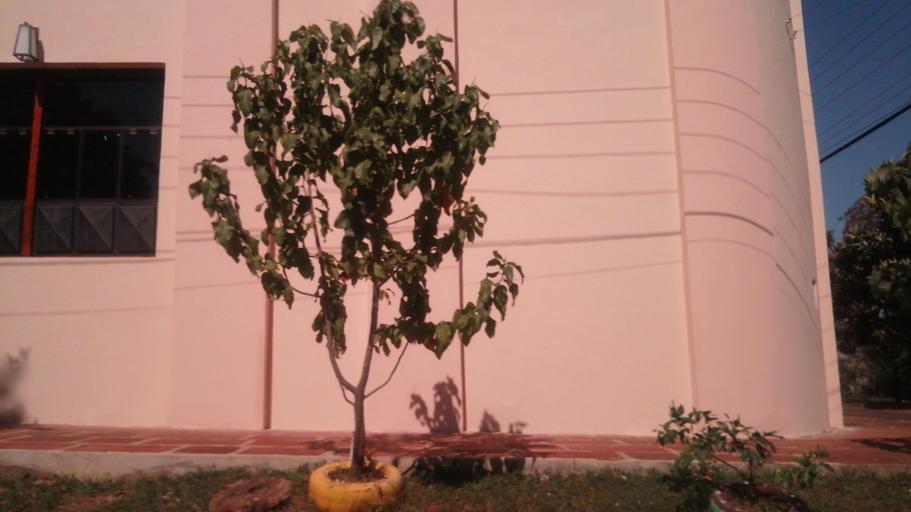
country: PY
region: Misiones
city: San Juan Bautista
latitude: -26.6670
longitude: -57.1499
